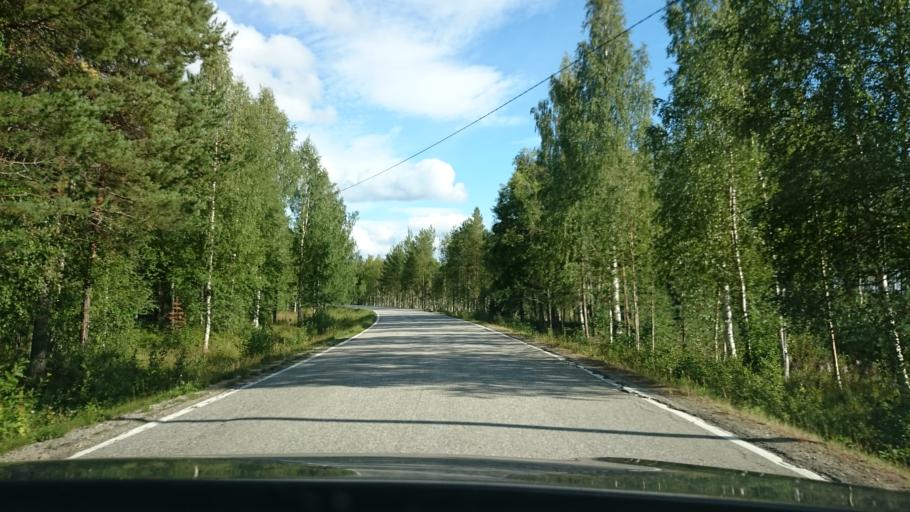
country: FI
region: Kainuu
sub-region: Kehys-Kainuu
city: Suomussalmi
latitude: 64.7582
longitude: 29.3901
